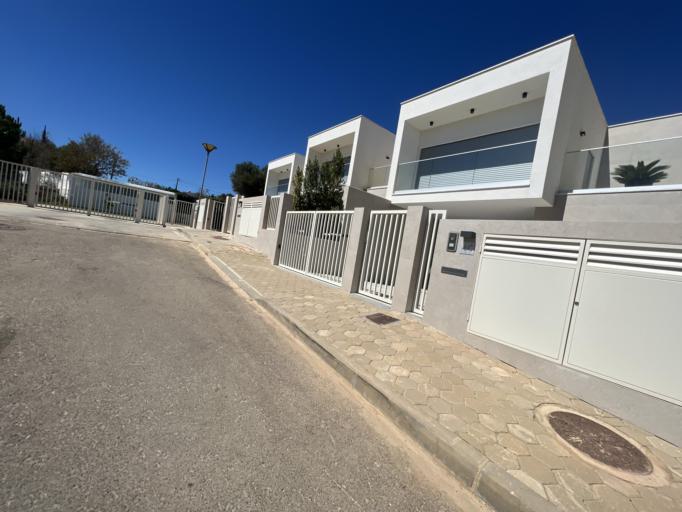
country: PT
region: Faro
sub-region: Portimao
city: Portimao
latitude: 37.1304
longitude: -8.5119
